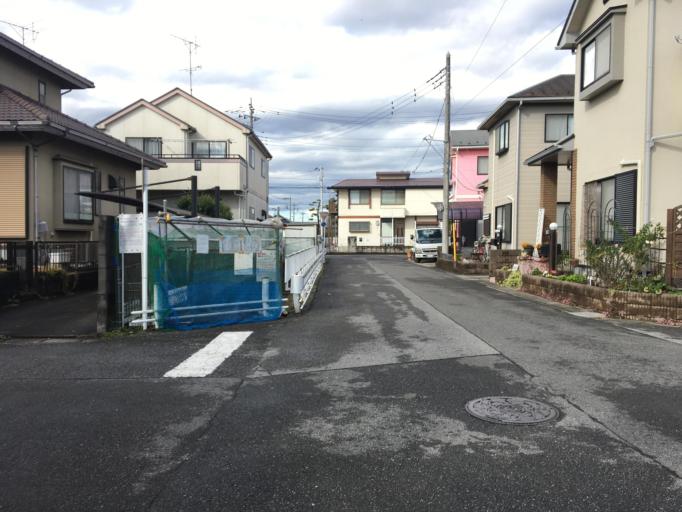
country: JP
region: Saitama
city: Koshigaya
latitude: 35.9236
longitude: 139.8092
